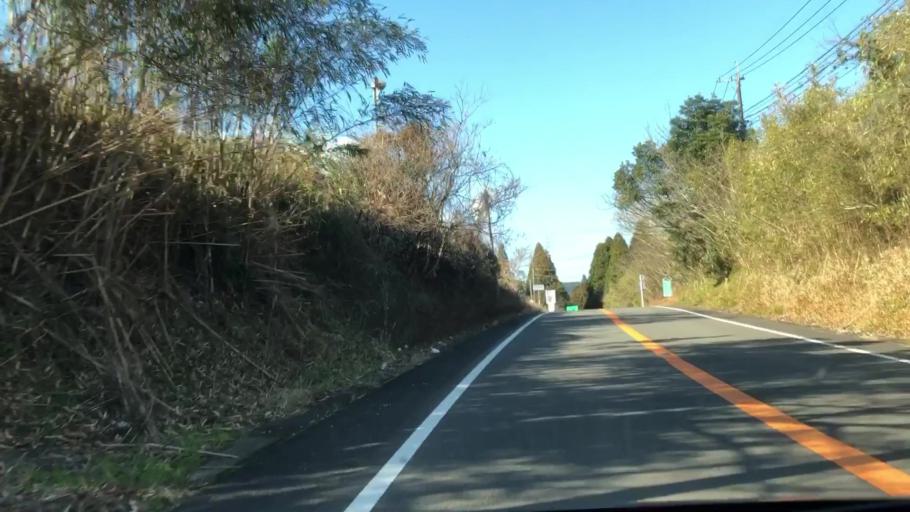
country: JP
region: Kagoshima
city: Satsumasendai
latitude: 31.8436
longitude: 130.4285
